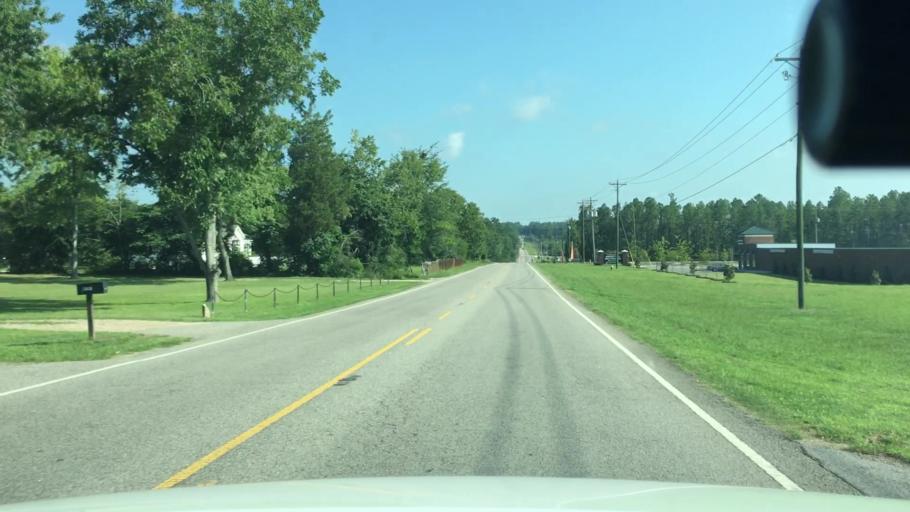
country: US
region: South Carolina
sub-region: Aiken County
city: Graniteville
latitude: 33.5779
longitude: -81.8358
